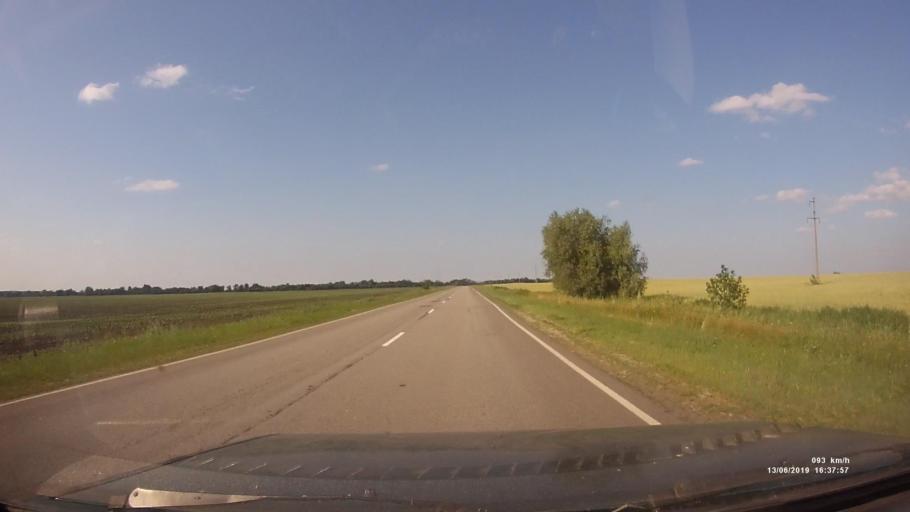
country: RU
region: Rostov
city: Kazanskaya
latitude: 49.9131
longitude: 41.3188
